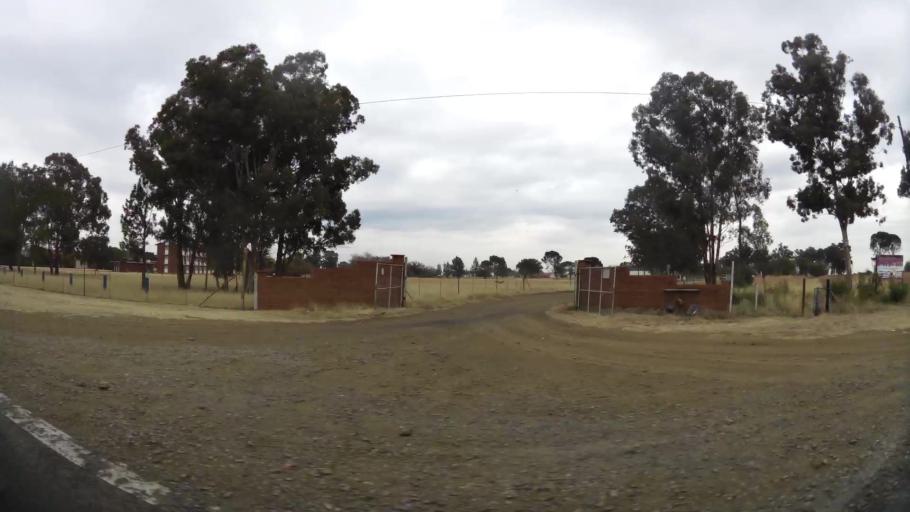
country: ZA
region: Orange Free State
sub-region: Fezile Dabi District Municipality
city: Kroonstad
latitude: -27.6216
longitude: 27.2333
